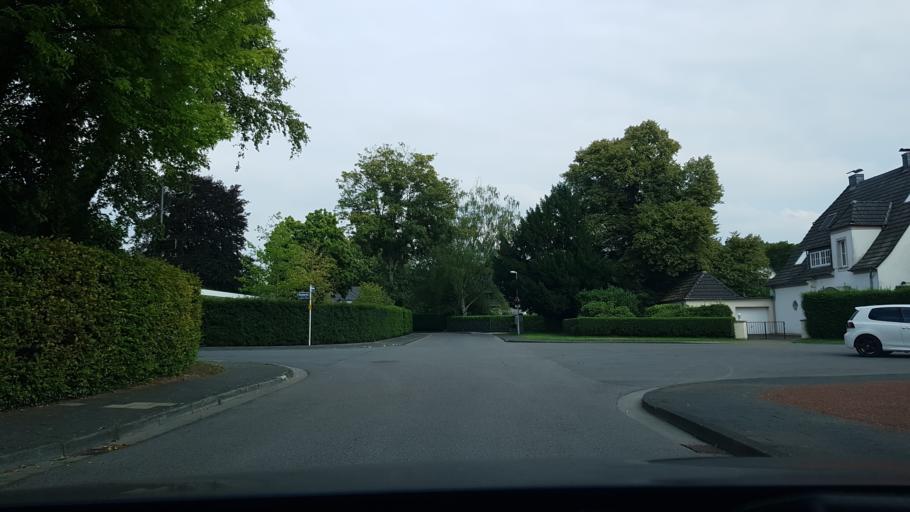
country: DE
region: North Rhine-Westphalia
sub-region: Regierungsbezirk Dusseldorf
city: Muelheim (Ruhr)
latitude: 51.4153
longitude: 6.8998
